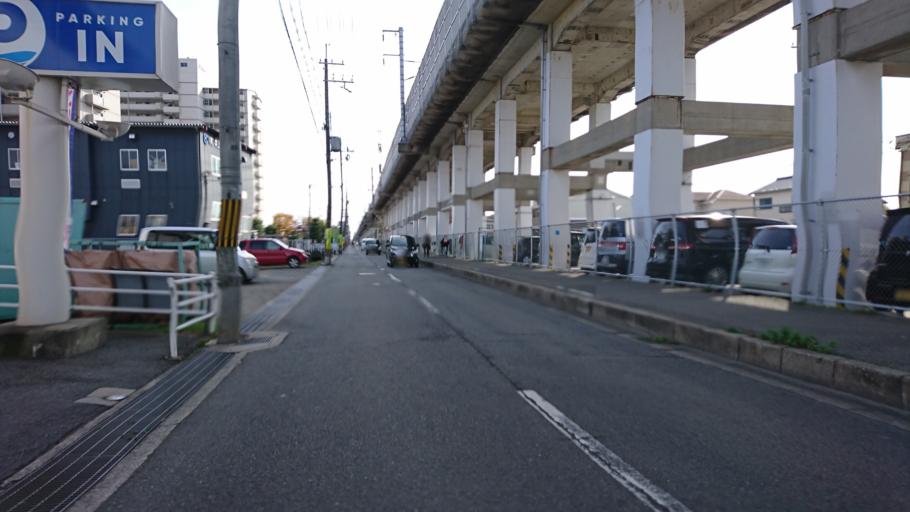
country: JP
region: Hyogo
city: Kakogawacho-honmachi
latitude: 34.7445
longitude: 134.8307
